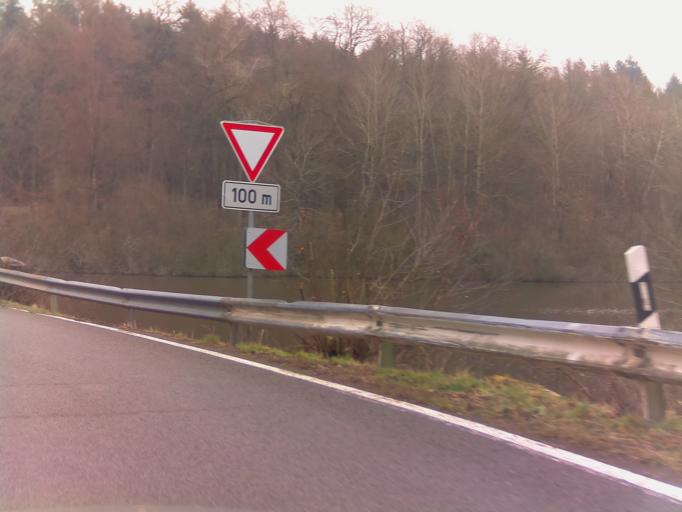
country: DE
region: Rheinland-Pfalz
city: Ruppertsecken
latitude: 49.6610
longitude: 7.9140
